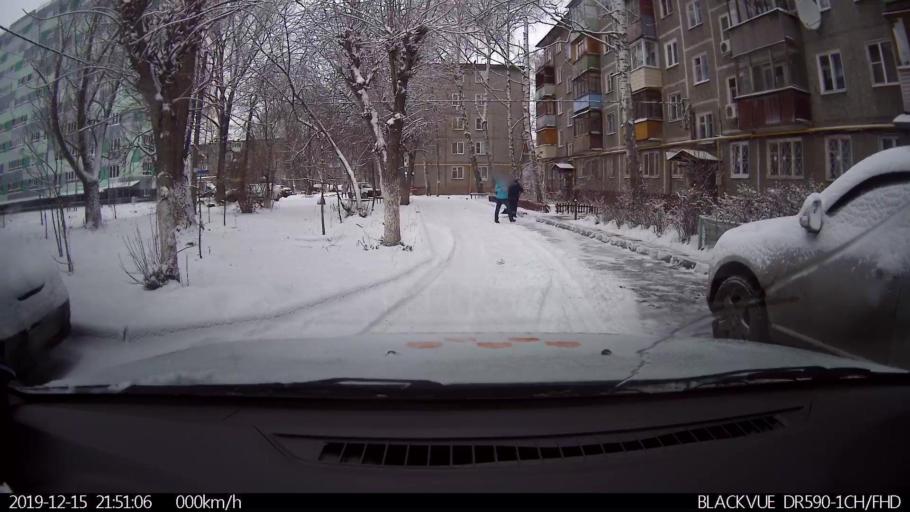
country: RU
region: Nizjnij Novgorod
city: Burevestnik
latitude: 56.2275
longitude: 43.8710
